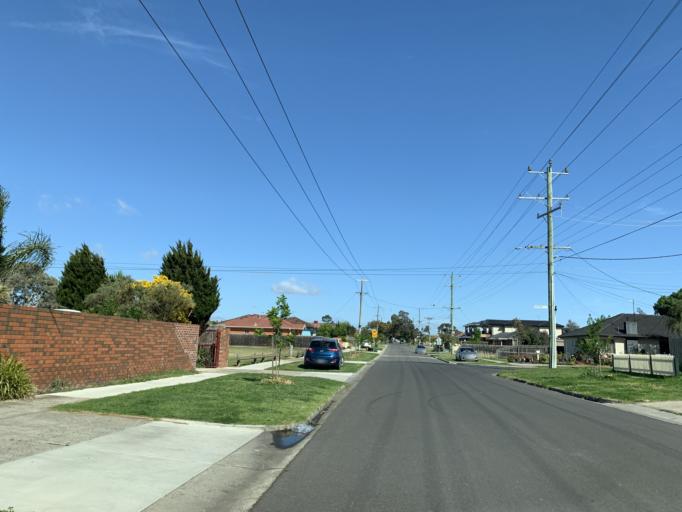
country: AU
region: Victoria
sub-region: Brimbank
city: Saint Albans
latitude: -37.7373
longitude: 144.8135
